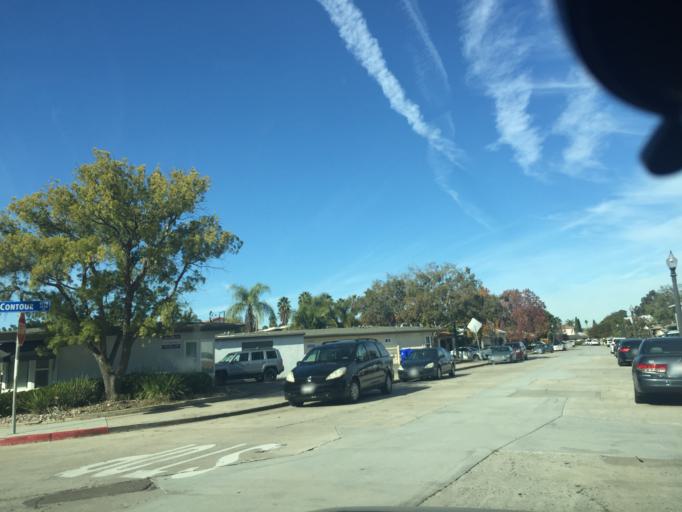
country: US
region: California
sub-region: San Diego County
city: Lemon Grove
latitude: 32.7590
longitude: -117.0819
